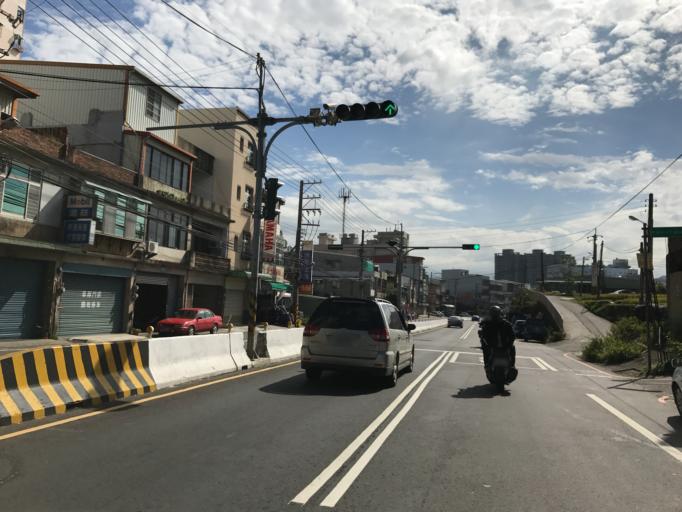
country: TW
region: Taiwan
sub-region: Hsinchu
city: Zhubei
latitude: 24.7632
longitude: 121.0602
